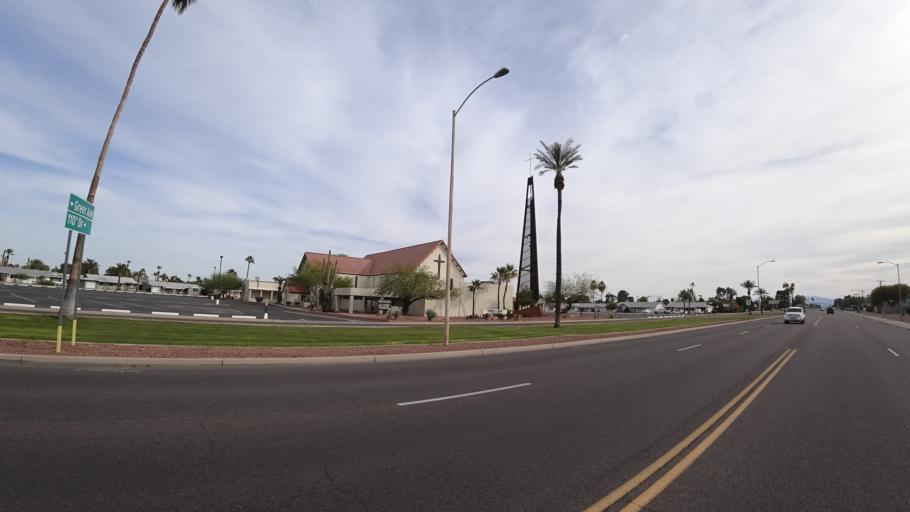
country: US
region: Arizona
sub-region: Maricopa County
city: Youngtown
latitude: 33.5848
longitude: -112.2988
